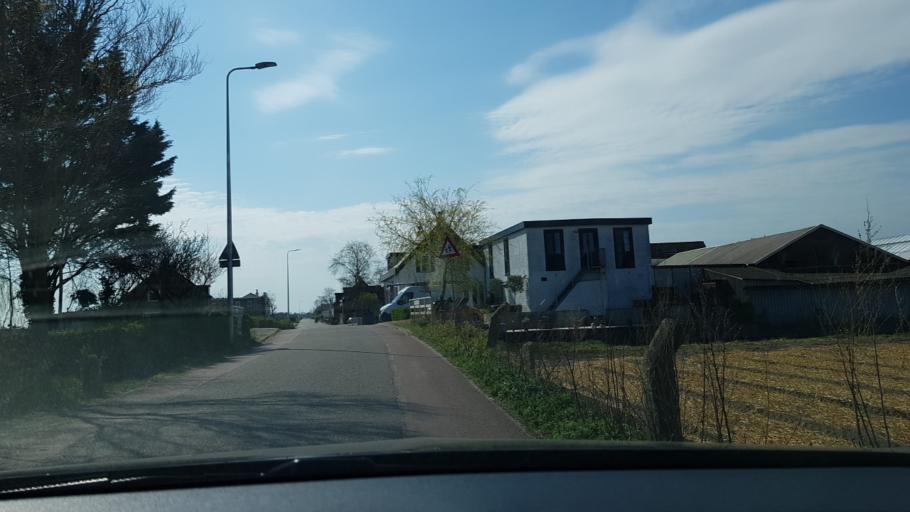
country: NL
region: South Holland
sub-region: Gemeente Teylingen
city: Sassenheim
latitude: 52.2499
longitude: 4.5208
